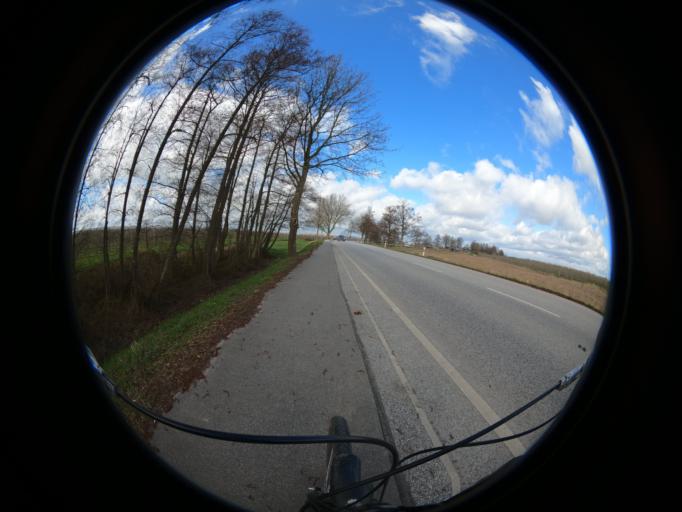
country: DE
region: Lower Saxony
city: Neu Wulmstorf
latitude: 53.5073
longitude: 9.7871
